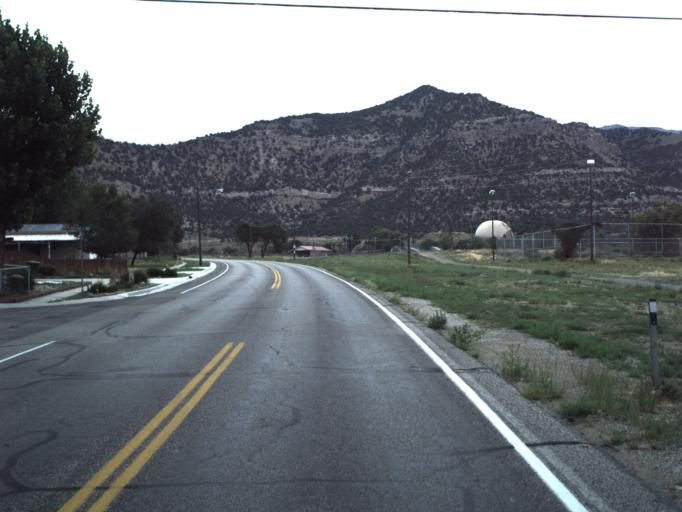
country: US
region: Utah
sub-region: Carbon County
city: East Carbon City
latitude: 39.5496
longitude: -110.3921
